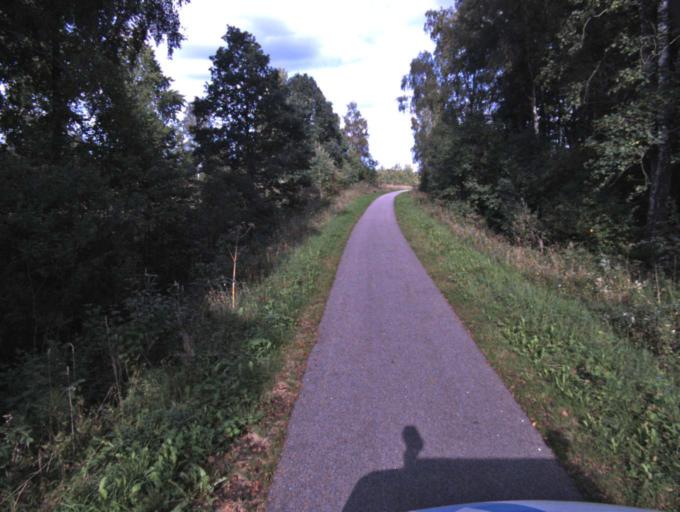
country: SE
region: Vaestra Goetaland
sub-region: Ulricehamns Kommun
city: Ulricehamn
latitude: 57.8962
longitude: 13.4464
